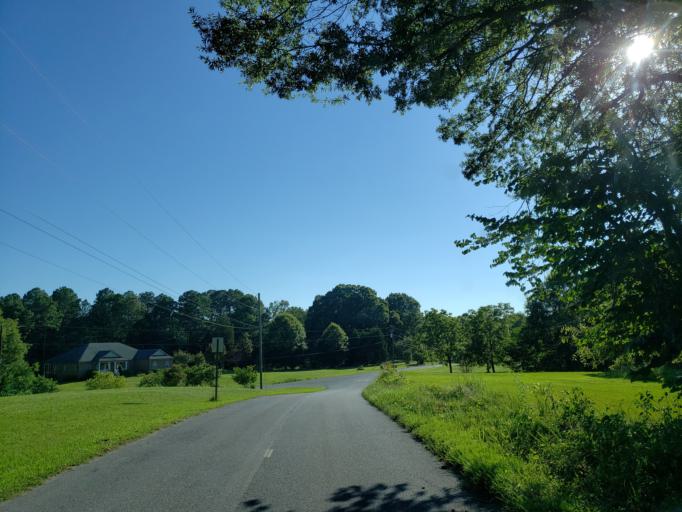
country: US
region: Georgia
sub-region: Polk County
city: Aragon
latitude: 34.1181
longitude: -85.0447
